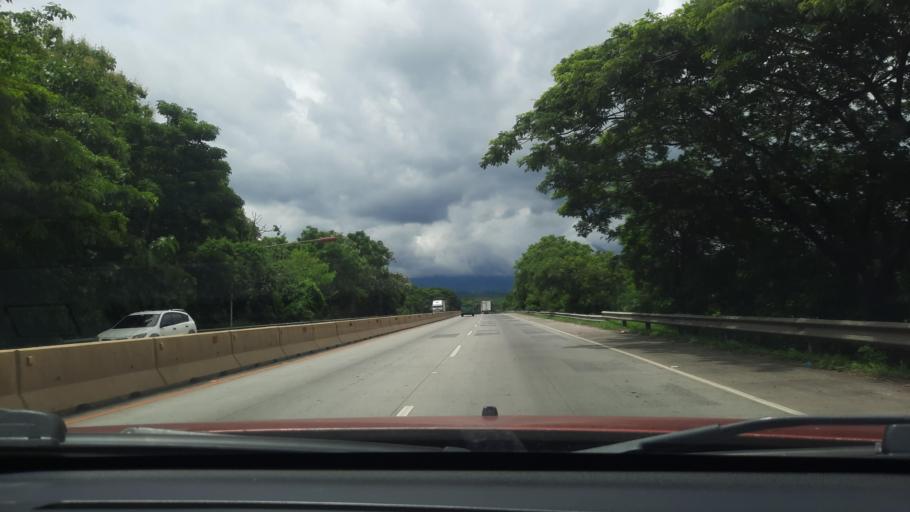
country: SV
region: Sonsonate
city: Sonzacate
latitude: 13.7202
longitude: -89.7067
